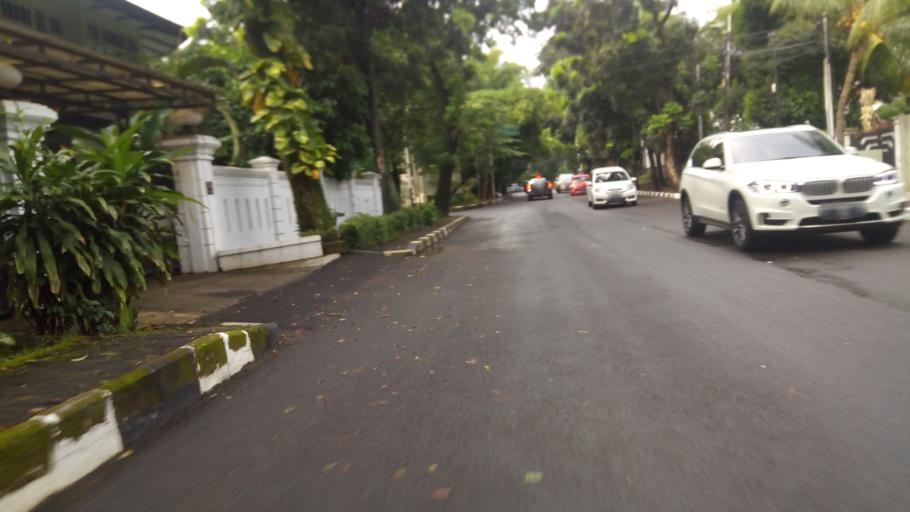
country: ID
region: Jakarta Raya
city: Jakarta
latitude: -6.2562
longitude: 106.8041
